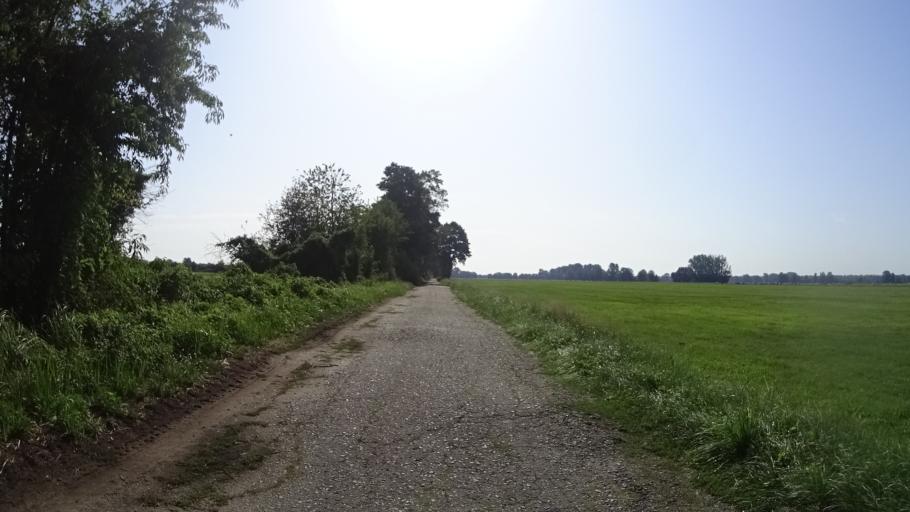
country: DE
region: Brandenburg
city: Neu Zauche
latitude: 51.9145
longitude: 14.0441
